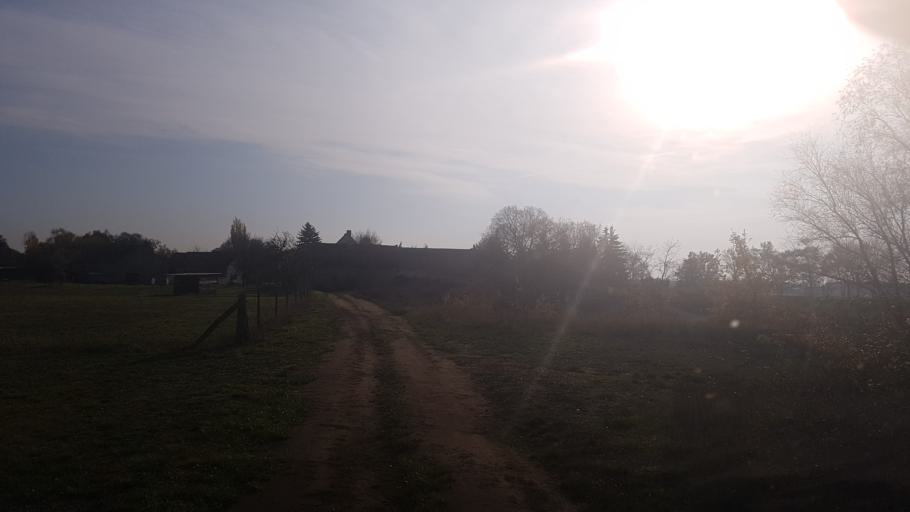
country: DE
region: Brandenburg
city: Schilda
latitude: 51.6085
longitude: 13.3118
